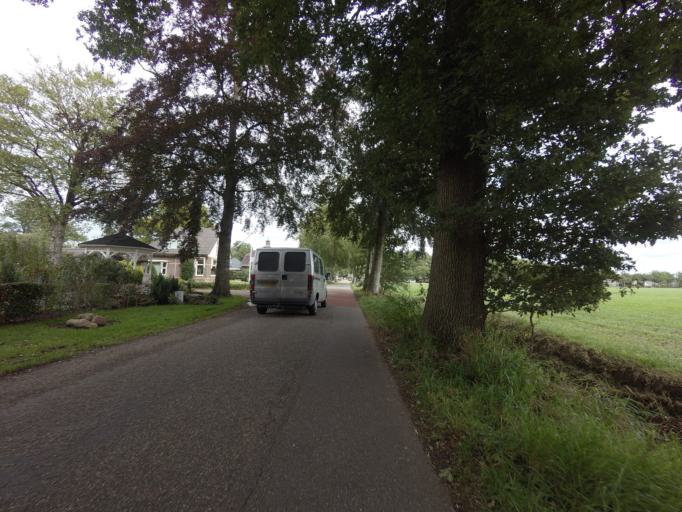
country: NL
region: Friesland
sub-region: Gemeente Weststellingwerf
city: Noordwolde
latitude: 52.9369
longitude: 6.1257
